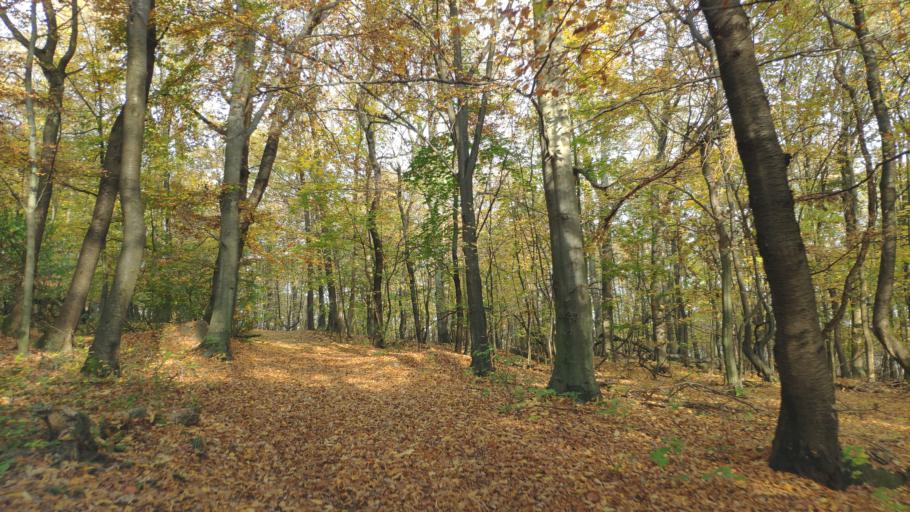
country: SK
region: Kosicky
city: Kosice
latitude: 48.7457
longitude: 21.2261
